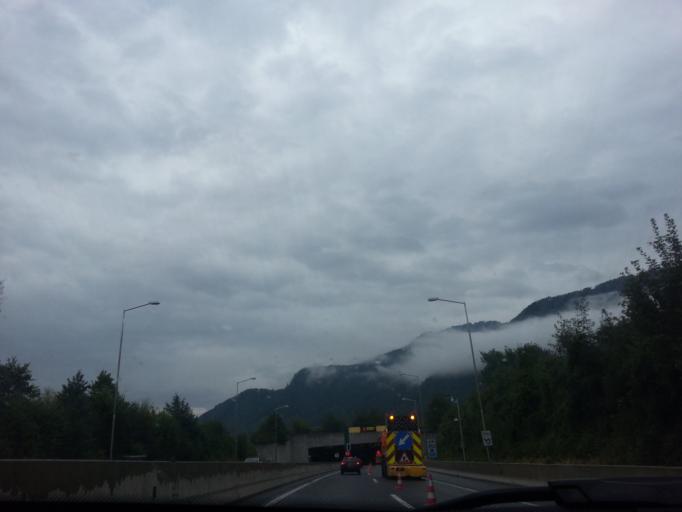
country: AT
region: Upper Austria
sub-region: Politischer Bezirk Kirchdorf an der Krems
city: Micheldorf in Oberoesterreich
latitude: 47.8926
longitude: 14.1052
